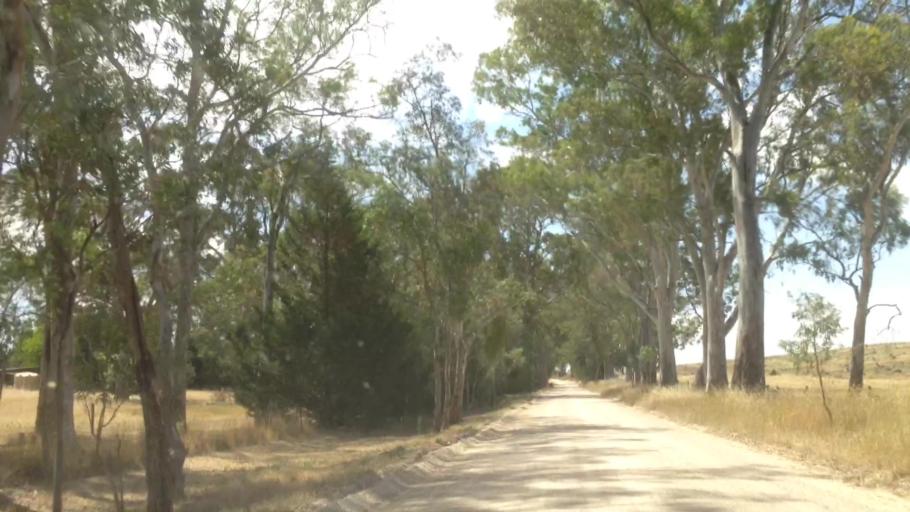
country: AU
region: South Australia
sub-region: Adelaide Hills
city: Birdwood
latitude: -34.7269
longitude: 138.9644
